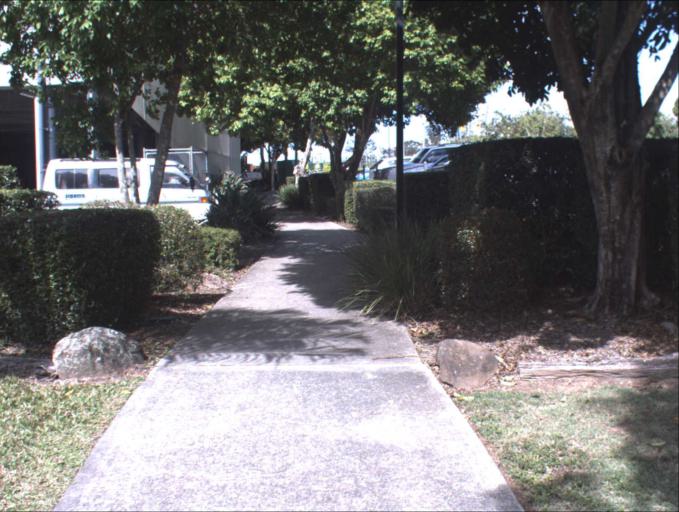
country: AU
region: Queensland
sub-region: Logan
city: Park Ridge South
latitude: -27.6685
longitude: 153.0308
